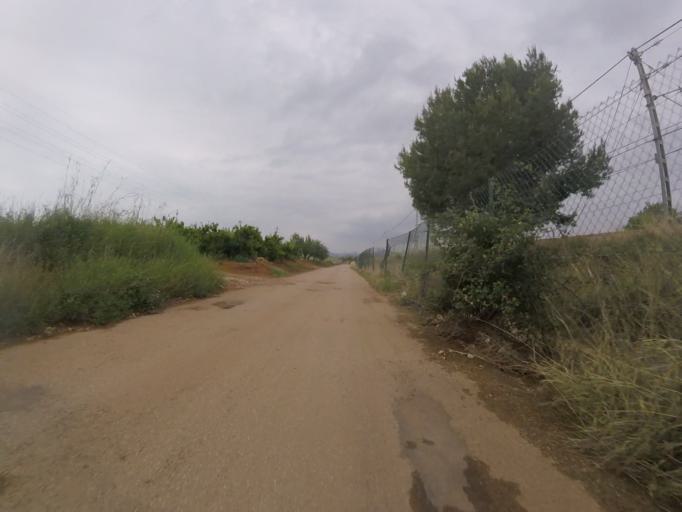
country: ES
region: Valencia
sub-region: Provincia de Castello
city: Torreblanca
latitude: 40.2165
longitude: 0.2041
